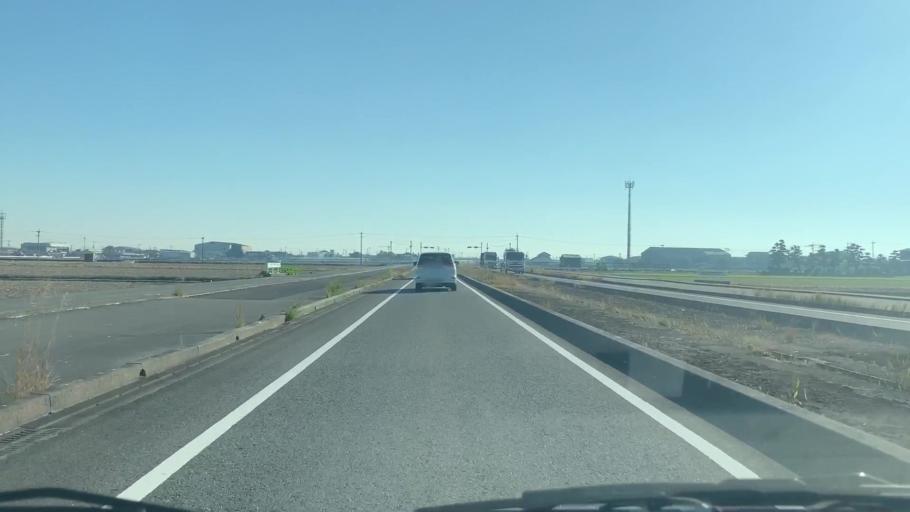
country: JP
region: Saga Prefecture
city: Saga-shi
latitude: 33.2214
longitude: 130.2015
